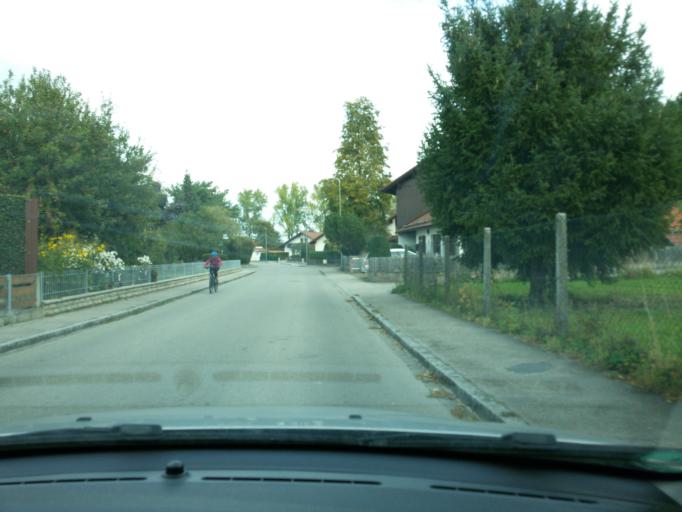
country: DE
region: Bavaria
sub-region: Swabia
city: Buchloe
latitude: 48.0417
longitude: 10.7320
